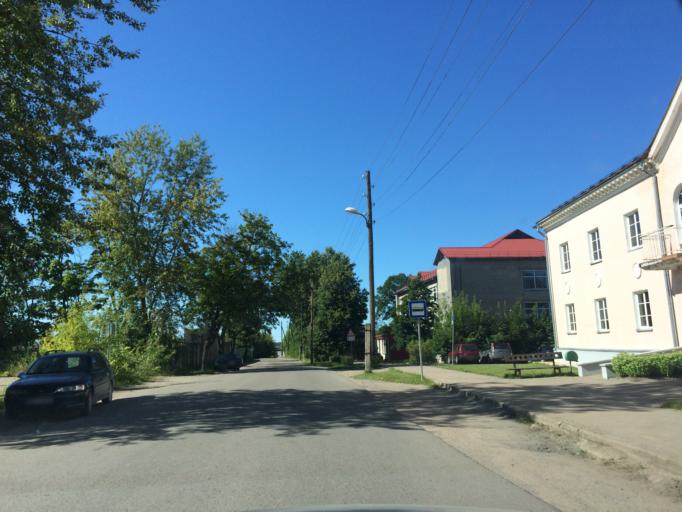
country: LV
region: Rezekne
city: Rezekne
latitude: 56.5041
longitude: 27.3205
